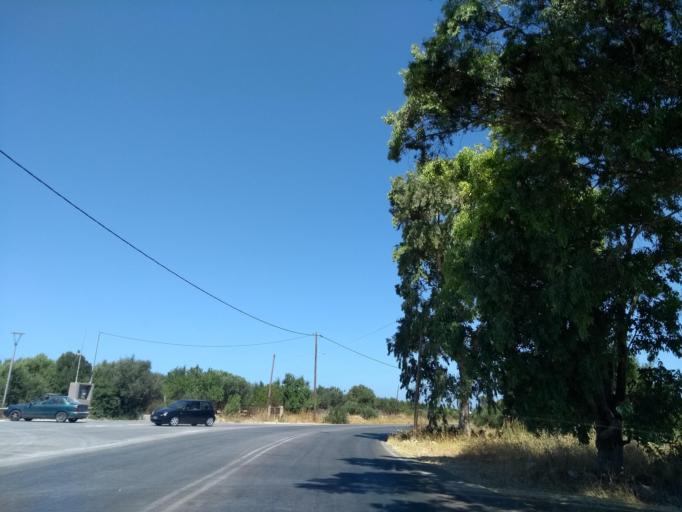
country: GR
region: Crete
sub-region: Nomos Chanias
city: Mouzouras
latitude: 35.5408
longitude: 24.1297
